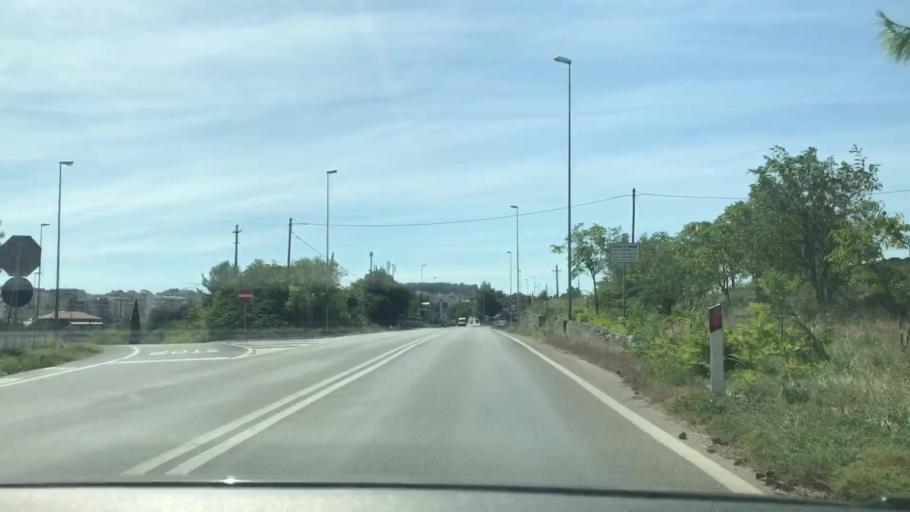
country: IT
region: Basilicate
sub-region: Provincia di Matera
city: Matera
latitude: 40.6854
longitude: 16.5902
